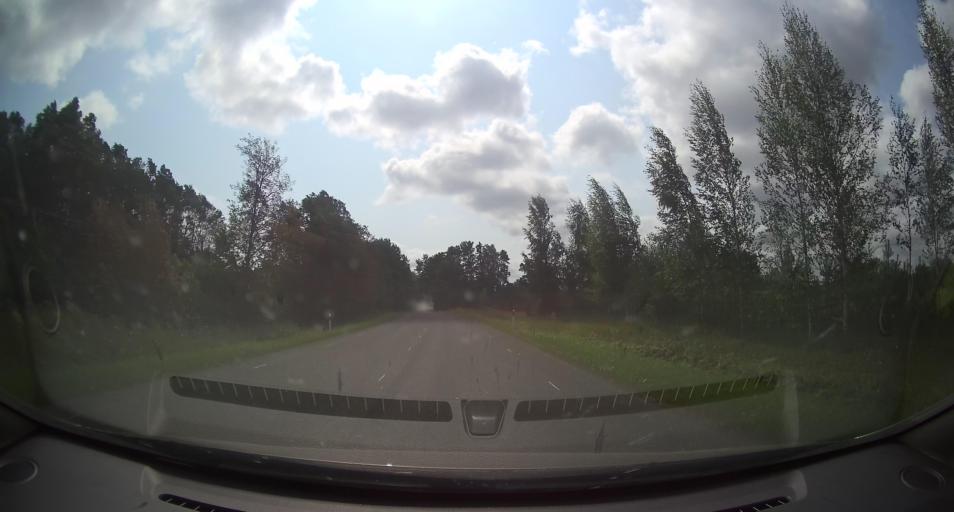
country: EE
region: Paernumaa
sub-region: Audru vald
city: Audru
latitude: 58.4939
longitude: 24.3357
